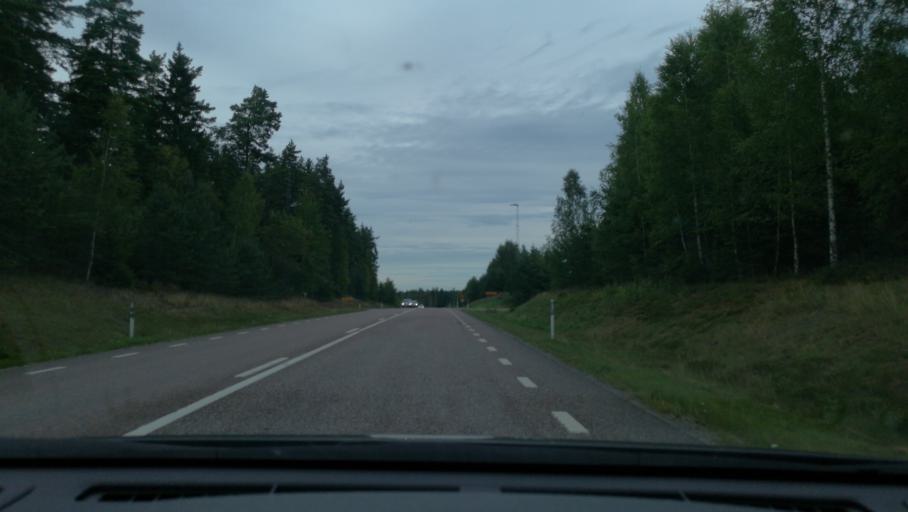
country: SE
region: Soedermanland
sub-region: Katrineholms Kommun
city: Katrineholm
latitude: 59.0402
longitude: 16.2177
